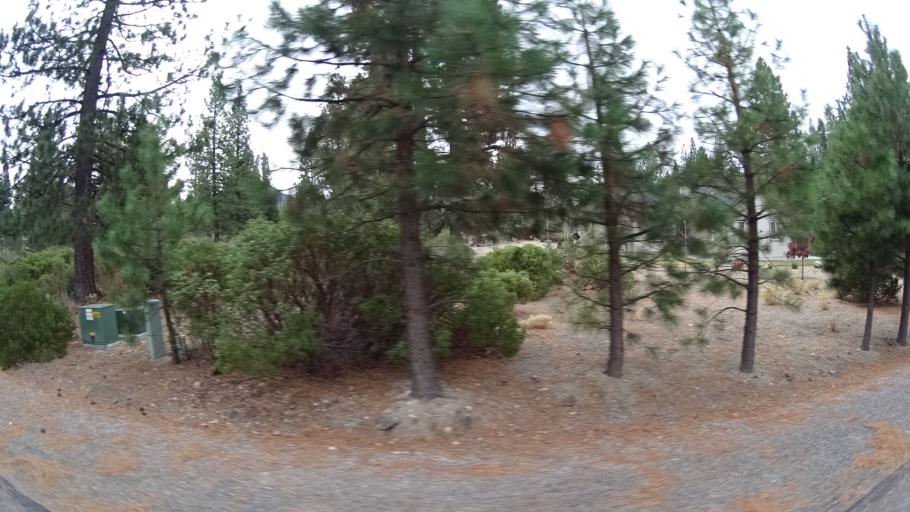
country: US
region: California
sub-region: Siskiyou County
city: Weed
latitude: 41.4083
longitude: -122.3723
